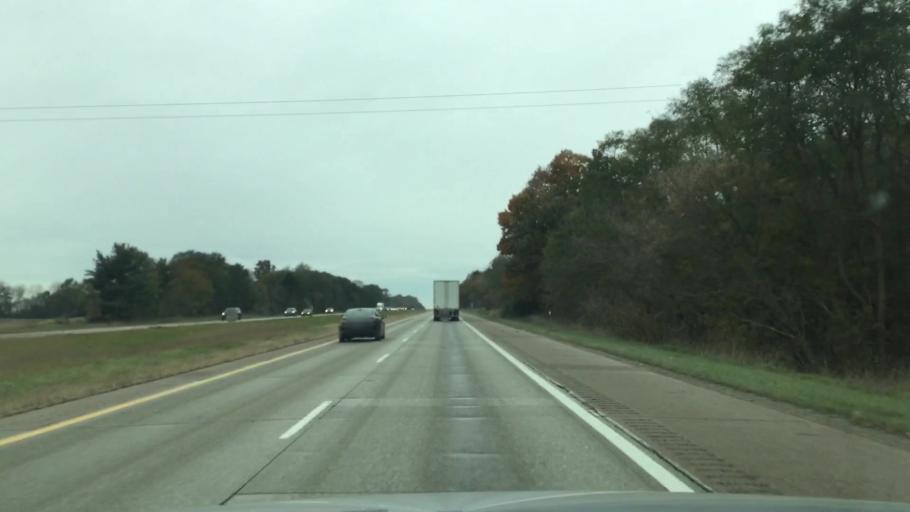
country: US
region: Michigan
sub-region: Jackson County
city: Concord
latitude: 42.2623
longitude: -84.6631
